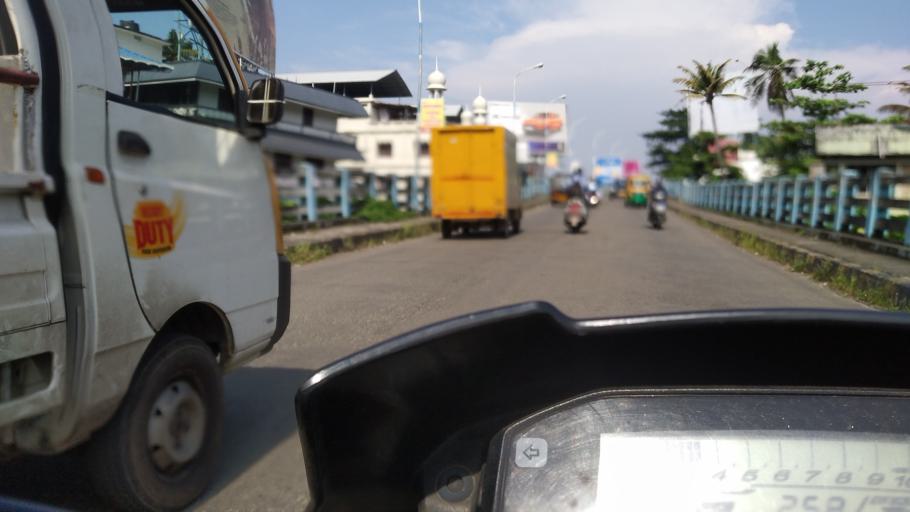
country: IN
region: Kerala
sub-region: Ernakulam
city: Cochin
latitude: 9.9824
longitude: 76.2871
